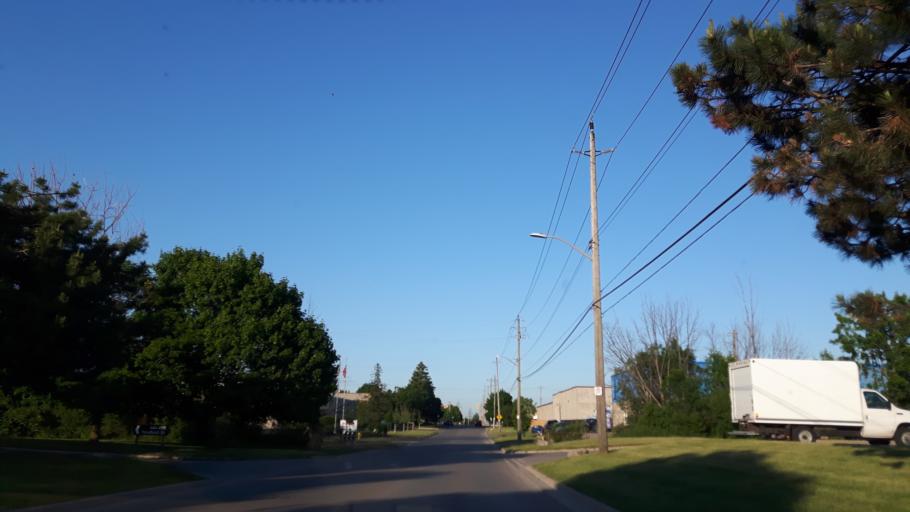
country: CA
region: Ontario
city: London
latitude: 42.9341
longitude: -81.2113
